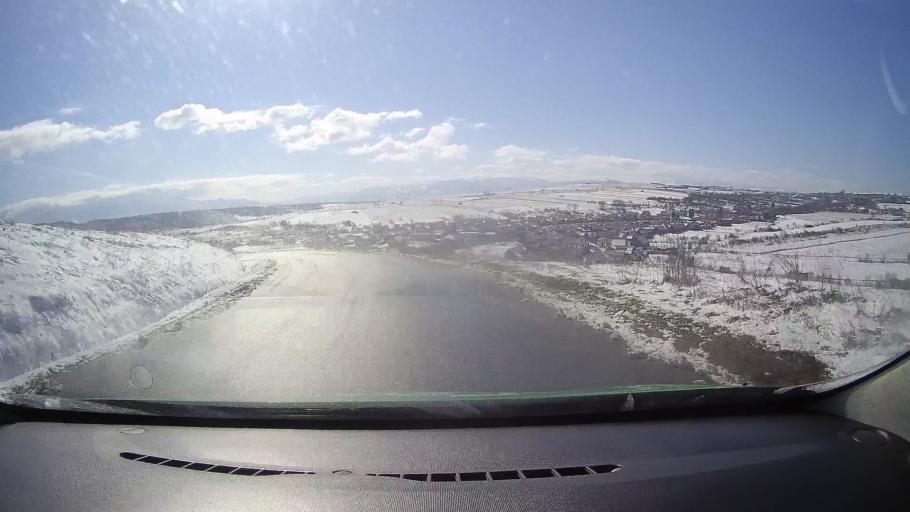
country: RO
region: Sibiu
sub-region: Comuna Rosia
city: Rosia
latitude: 45.8054
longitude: 24.2909
